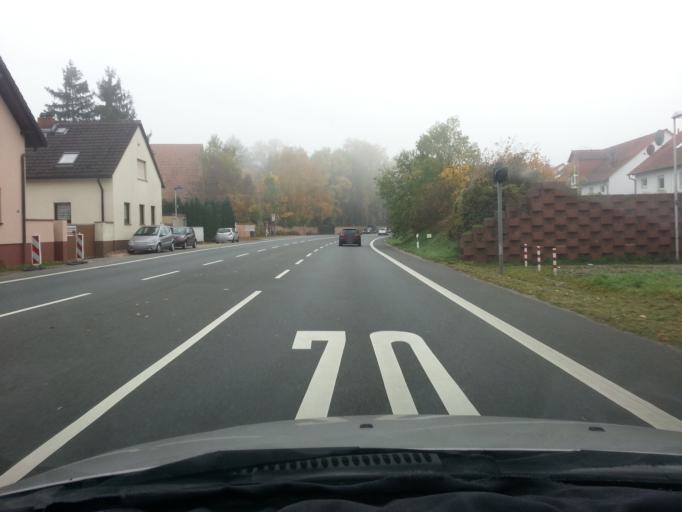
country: DE
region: Hesse
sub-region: Regierungsbezirk Darmstadt
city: Egelsbach
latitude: 49.9537
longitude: 8.6731
